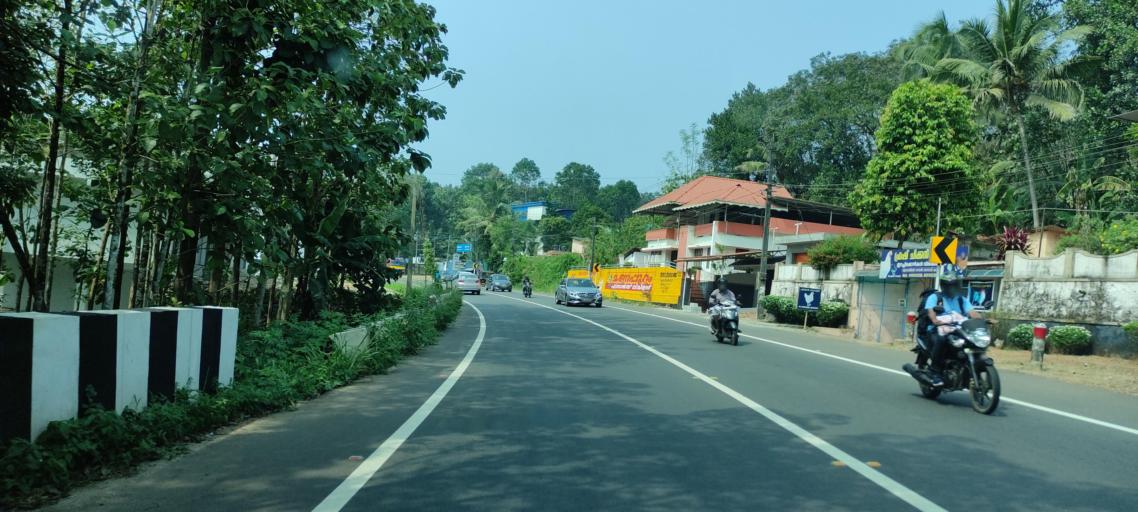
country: IN
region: Kerala
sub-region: Pattanamtitta
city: Adur
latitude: 9.1930
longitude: 76.7048
